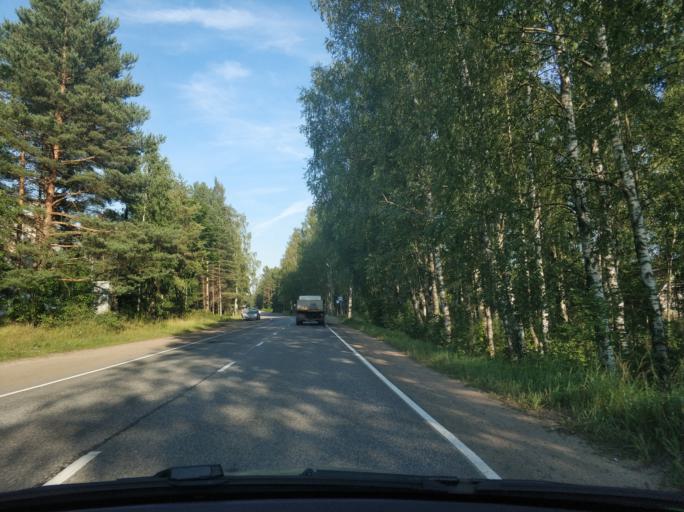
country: RU
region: Leningrad
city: Borisova Griva
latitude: 60.0931
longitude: 30.9832
